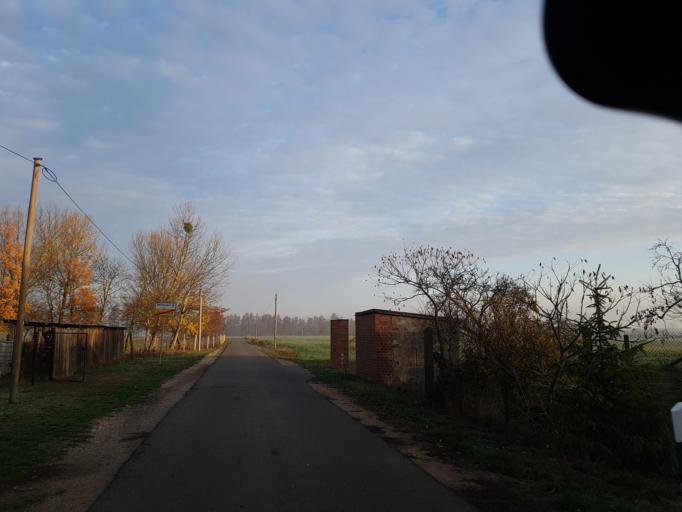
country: DE
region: Saxony-Anhalt
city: Elster
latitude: 51.8663
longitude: 12.8459
